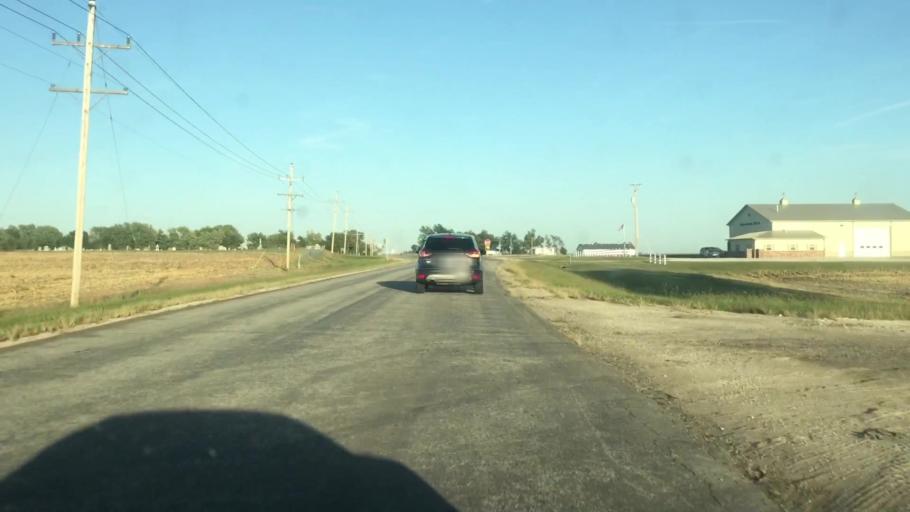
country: US
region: Kansas
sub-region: Atchison County
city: Atchison
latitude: 39.5651
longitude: -95.3086
